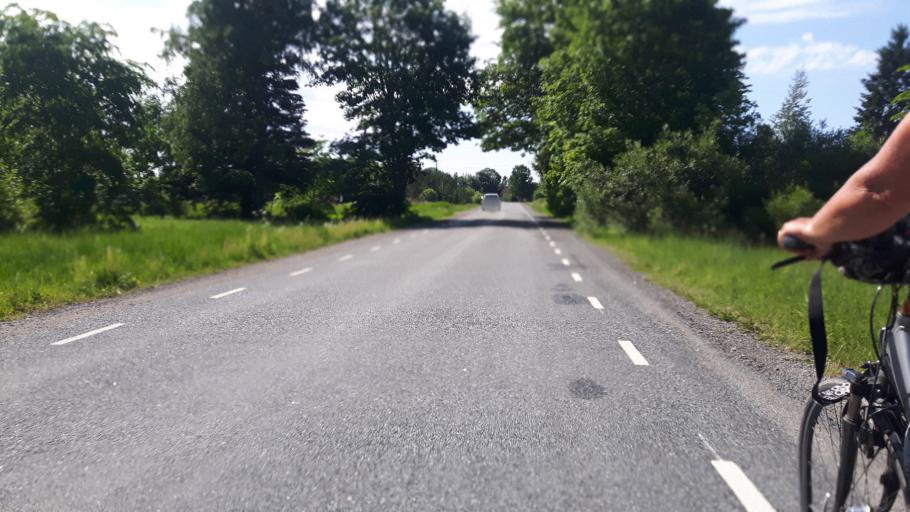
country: EE
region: Paernumaa
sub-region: Vaendra vald (alev)
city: Vandra
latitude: 58.6597
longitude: 25.0237
